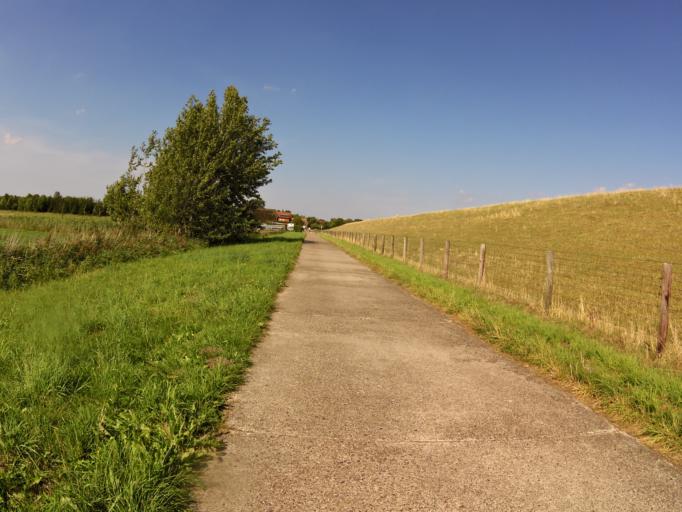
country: DE
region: Lower Saxony
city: Ovelgonne
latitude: 53.3912
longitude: 8.4593
